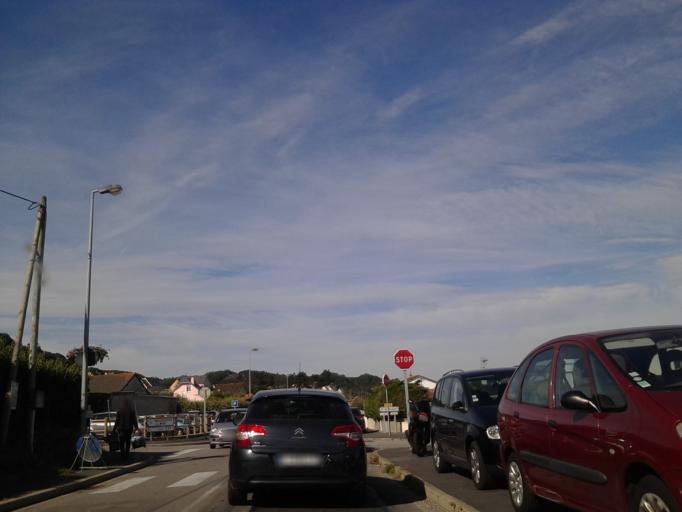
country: FR
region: Lower Normandy
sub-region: Departement de la Manche
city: Bretteville
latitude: 49.6572
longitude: -1.5196
